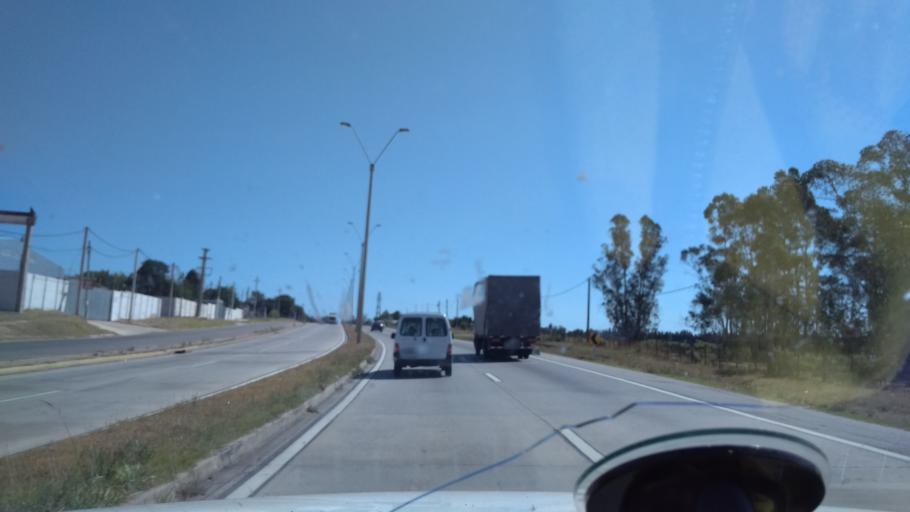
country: UY
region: Canelones
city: Toledo
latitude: -34.7906
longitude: -56.1110
